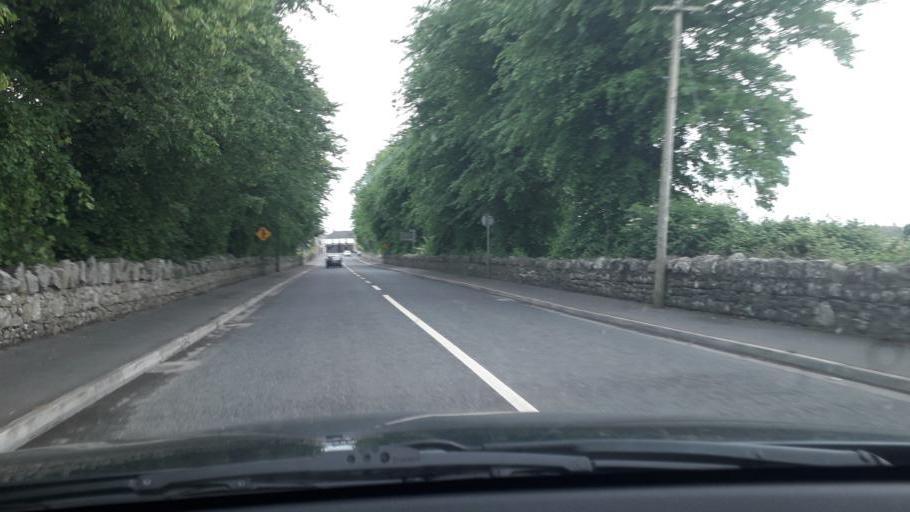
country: IE
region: Leinster
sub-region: Kildare
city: Castledermot
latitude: 52.9130
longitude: -6.8410
